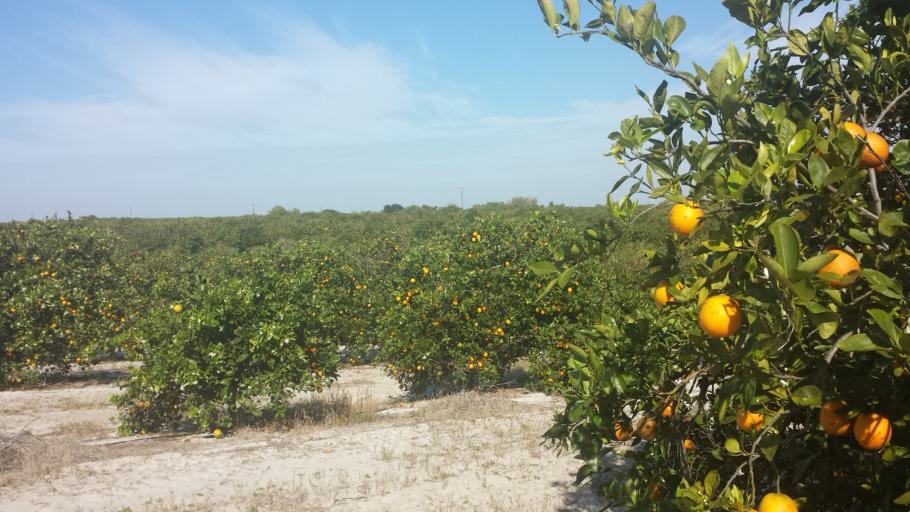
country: US
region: Florida
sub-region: Highlands County
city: Lake Placid
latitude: 27.2693
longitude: -81.3669
